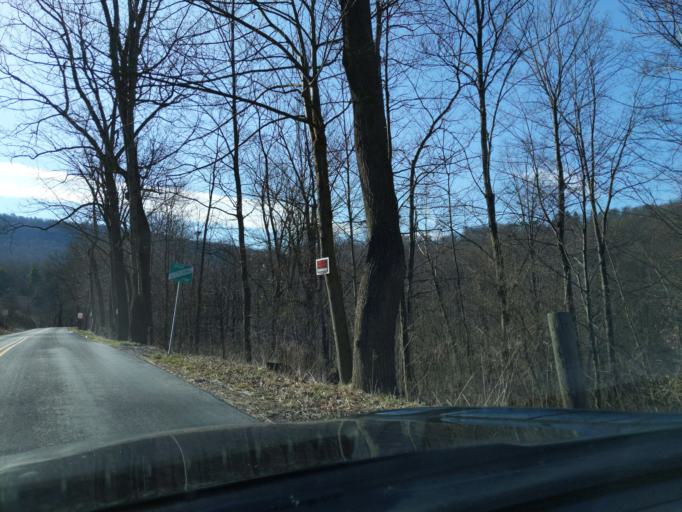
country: US
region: Pennsylvania
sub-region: Blair County
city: Hollidaysburg
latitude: 40.4050
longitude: -78.3196
